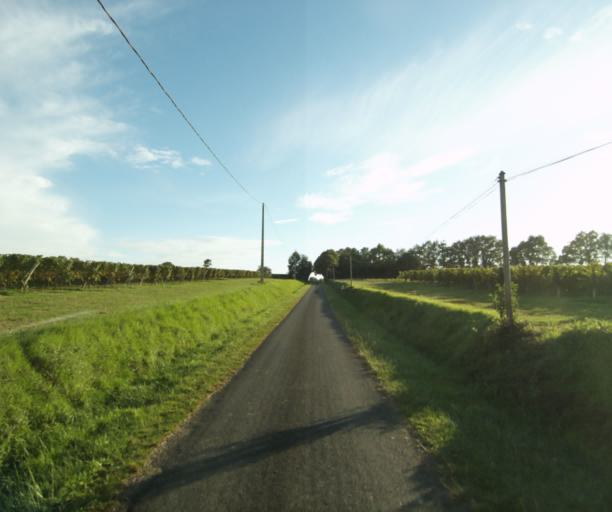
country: FR
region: Midi-Pyrenees
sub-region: Departement du Gers
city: Eauze
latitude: 43.8554
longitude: 0.0151
